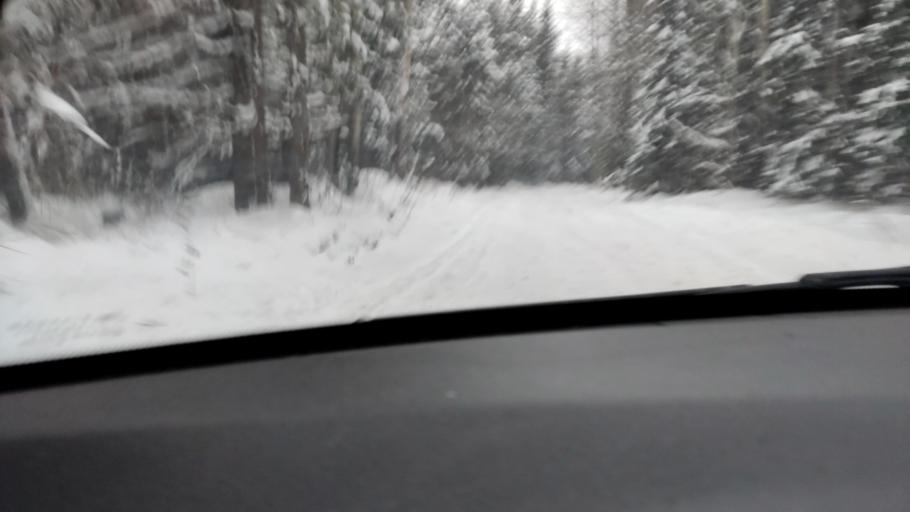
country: RU
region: Perm
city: Krasnokamsk
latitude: 57.9952
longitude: 55.7801
